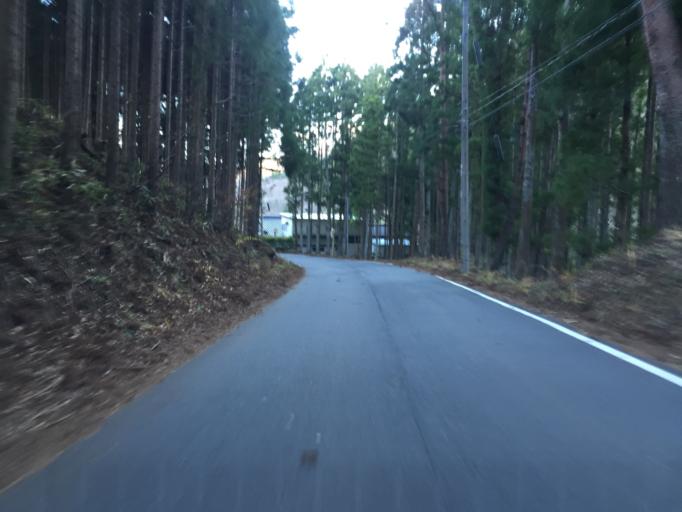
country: JP
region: Fukushima
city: Iwaki
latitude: 37.1844
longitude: 140.8167
